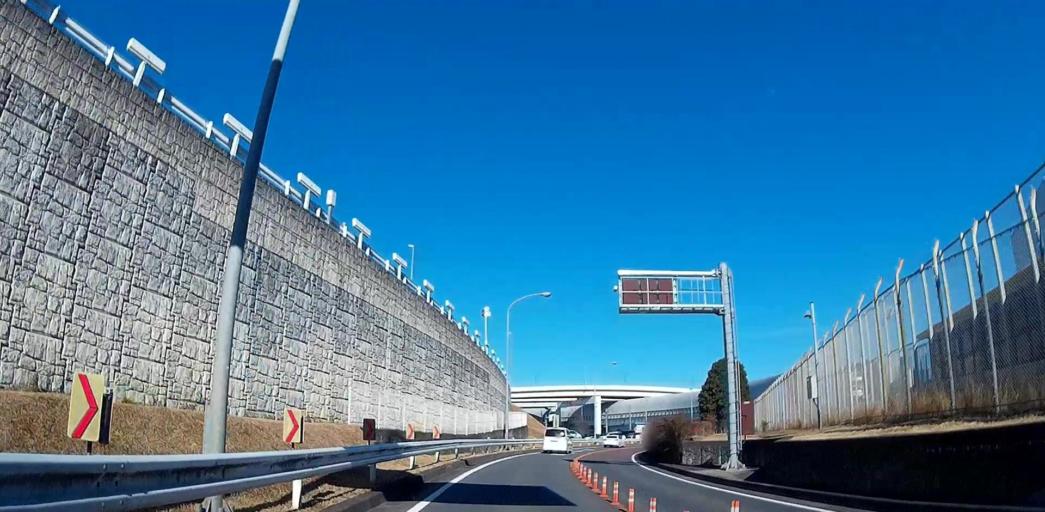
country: JP
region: Chiba
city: Narita
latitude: 35.7656
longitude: 140.3894
